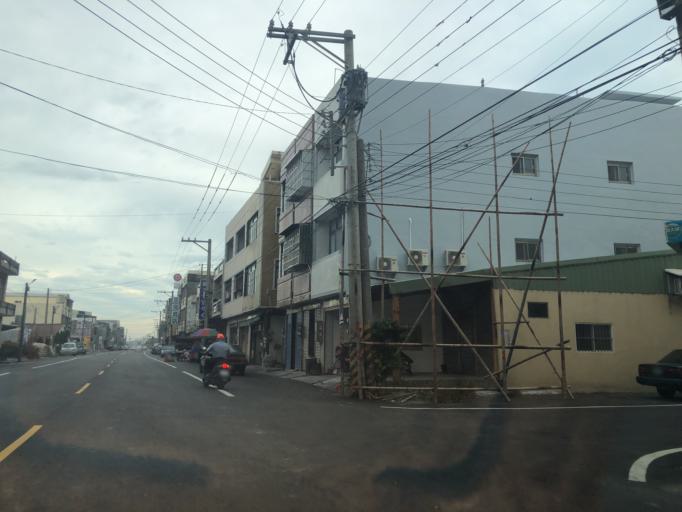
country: TW
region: Taiwan
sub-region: Chiayi
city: Taibao
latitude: 23.7023
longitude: 120.2001
